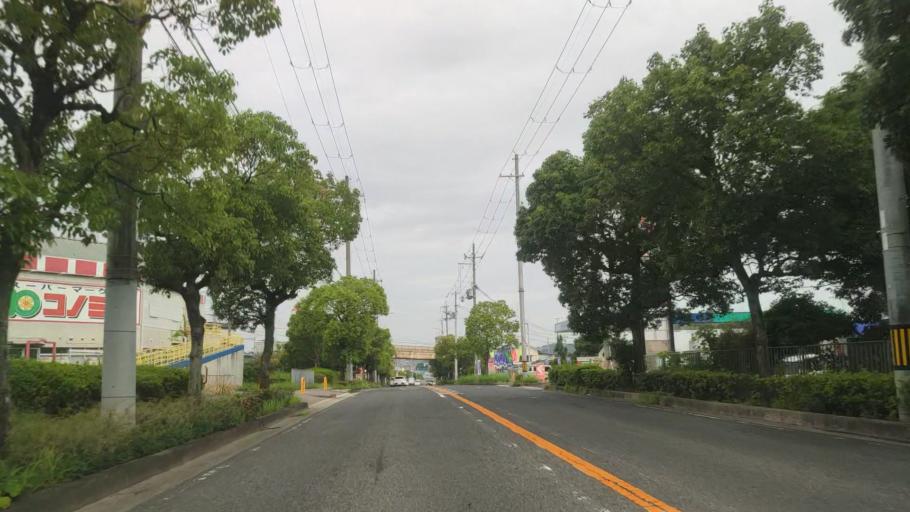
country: JP
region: Osaka
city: Tondabayashicho
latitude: 34.4263
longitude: 135.5714
